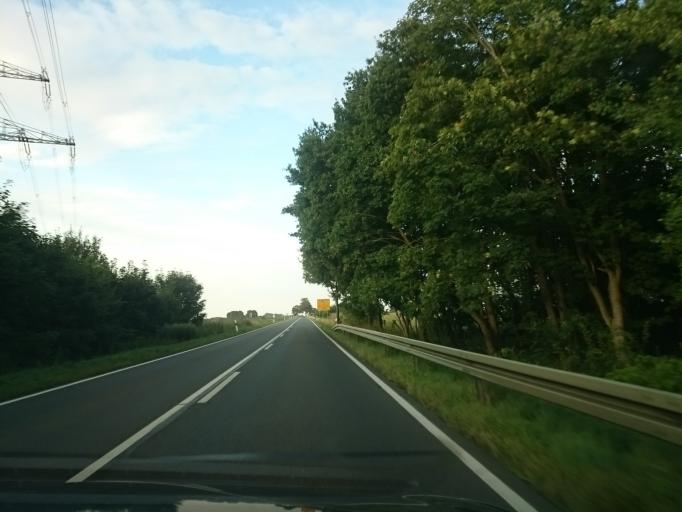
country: DE
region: Mecklenburg-Vorpommern
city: Zussow
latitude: 53.9604
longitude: 13.5178
